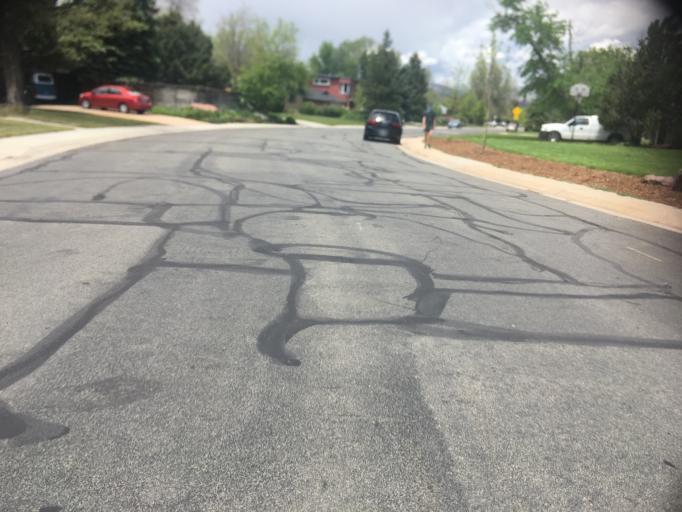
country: US
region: Colorado
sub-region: Boulder County
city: Boulder
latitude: 40.0010
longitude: -105.2298
